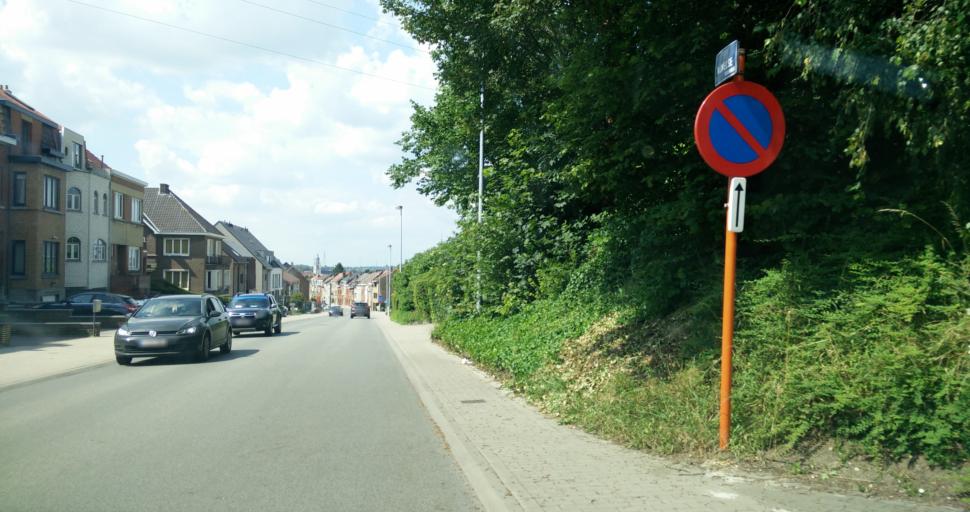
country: BE
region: Flanders
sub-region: Provincie Vlaams-Brabant
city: Halle
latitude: 50.7230
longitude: 4.2486
